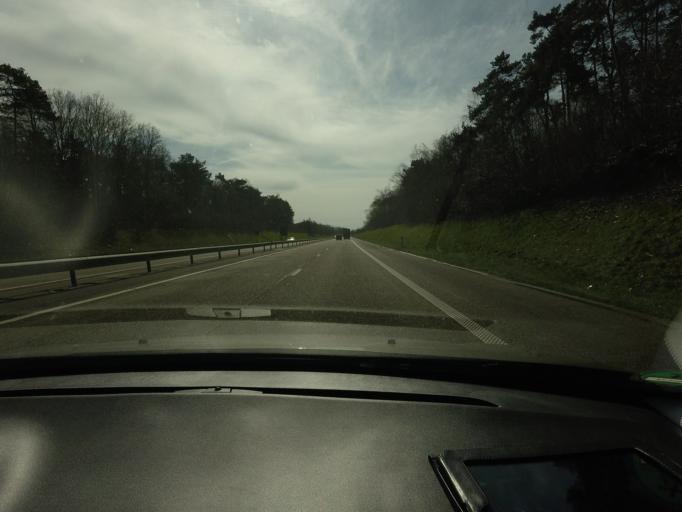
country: BE
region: Flanders
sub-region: Provincie Limburg
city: Overpelt
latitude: 51.1664
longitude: 5.4059
